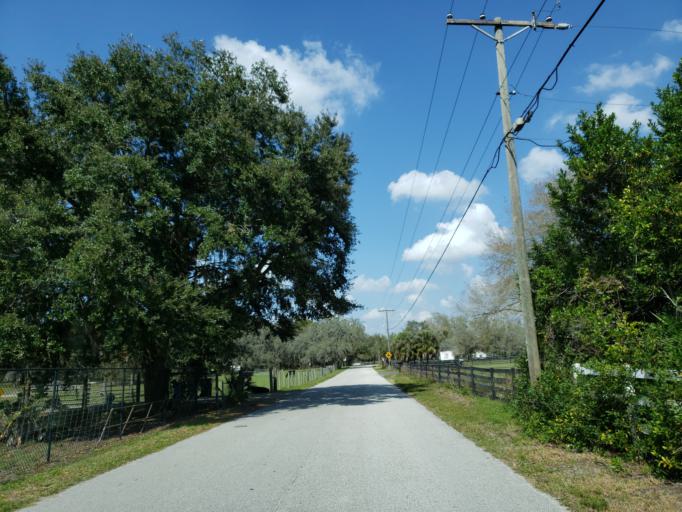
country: US
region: Florida
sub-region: Hillsborough County
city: Keystone
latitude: 28.1493
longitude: -82.6408
